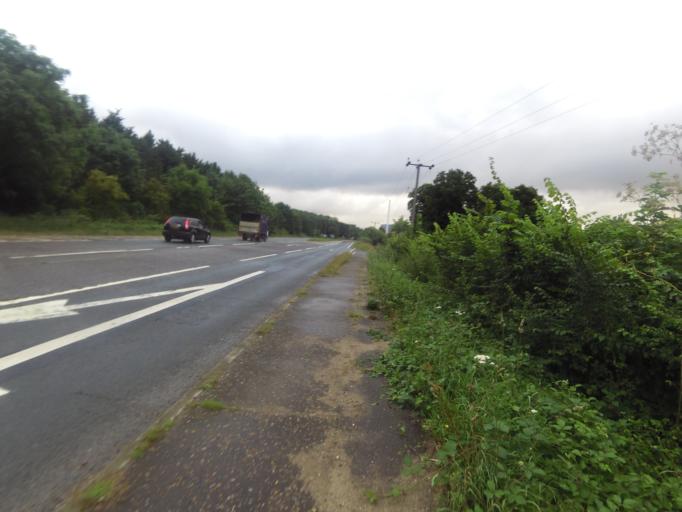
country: GB
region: England
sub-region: Suffolk
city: Bramford
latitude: 52.0987
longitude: 1.0951
